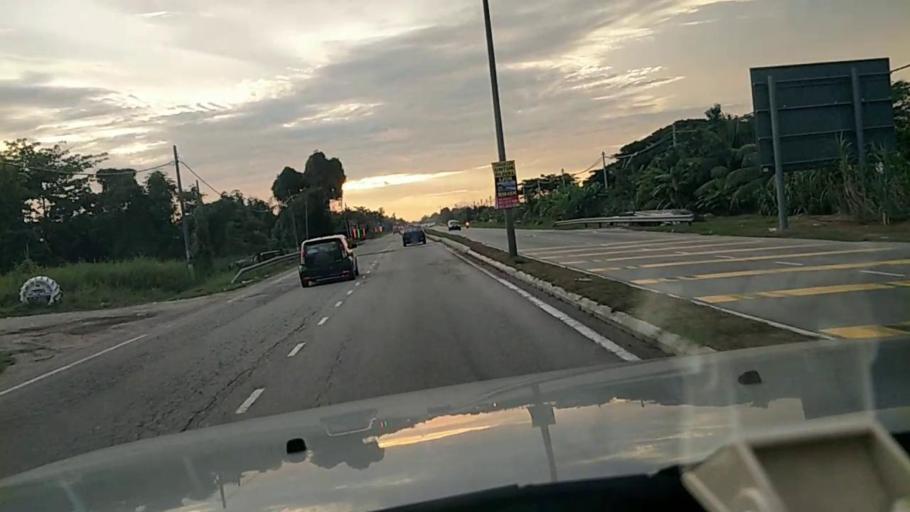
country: MY
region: Perak
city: Kampong Dungun
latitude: 3.1401
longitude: 101.3664
